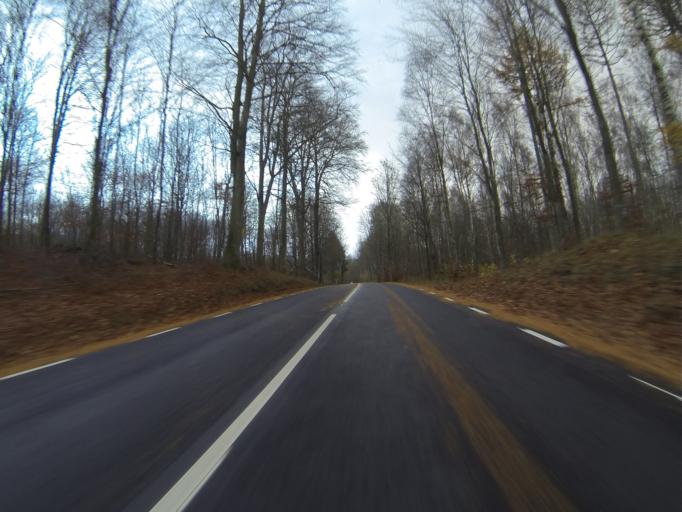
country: SE
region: Skane
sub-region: Lunds Kommun
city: Genarp
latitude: 55.5918
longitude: 13.4177
